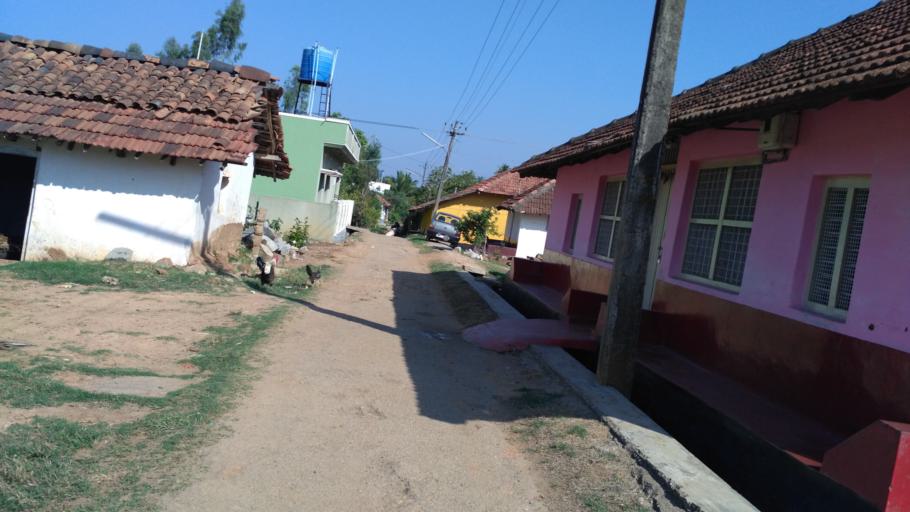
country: IN
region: Karnataka
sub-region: Hassan
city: Hassan
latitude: 12.9999
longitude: 76.1267
